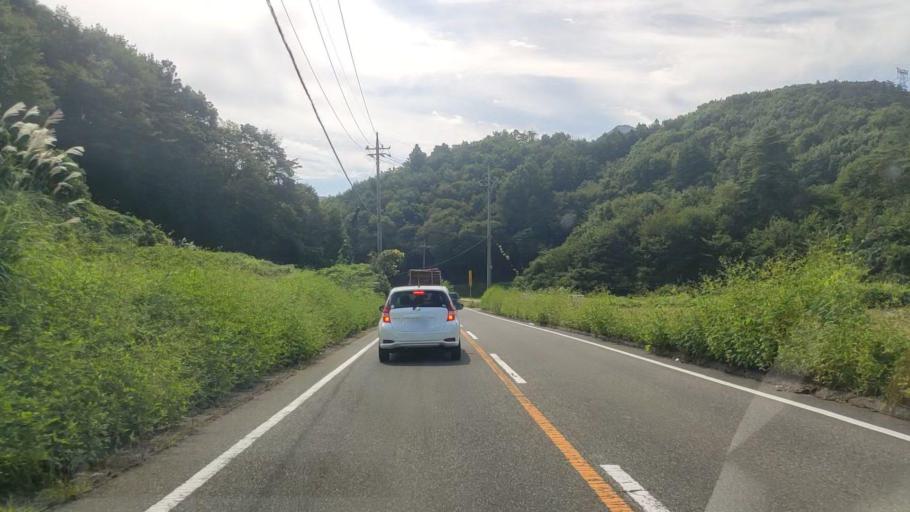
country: JP
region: Gunma
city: Numata
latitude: 36.6300
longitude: 138.9969
